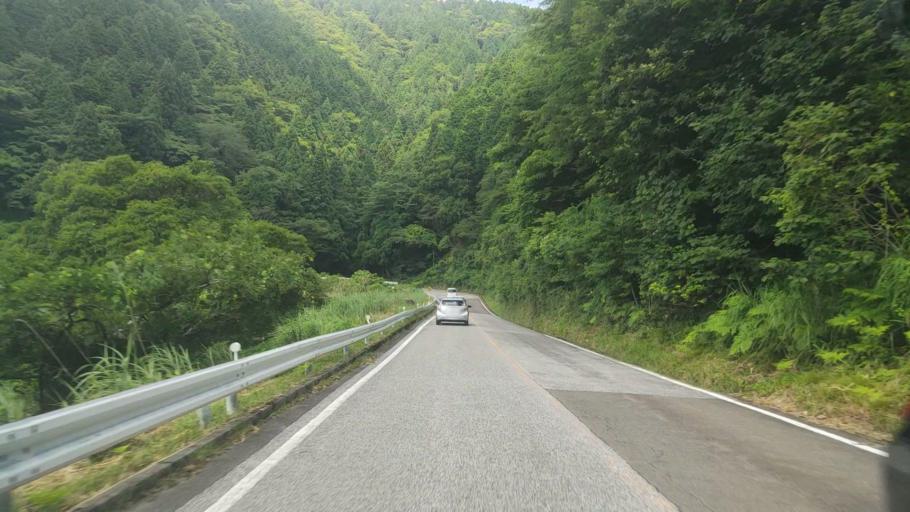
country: JP
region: Gifu
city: Tarui
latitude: 35.3838
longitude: 136.4469
